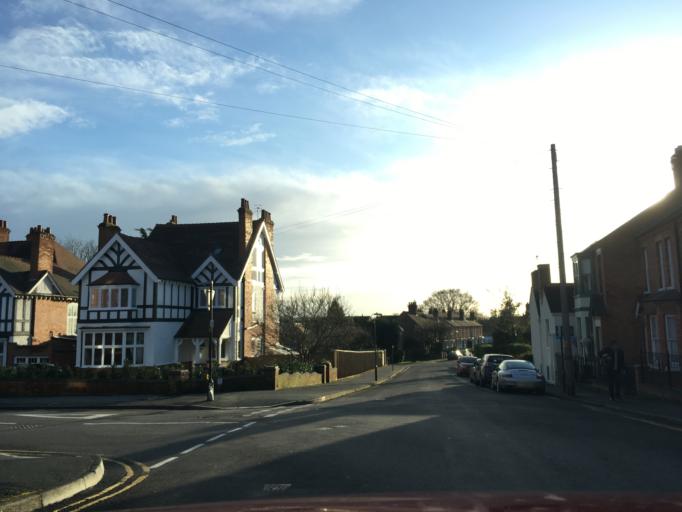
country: GB
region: England
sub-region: Warwickshire
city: Stratford-upon-Avon
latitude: 52.1974
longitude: -1.7050
